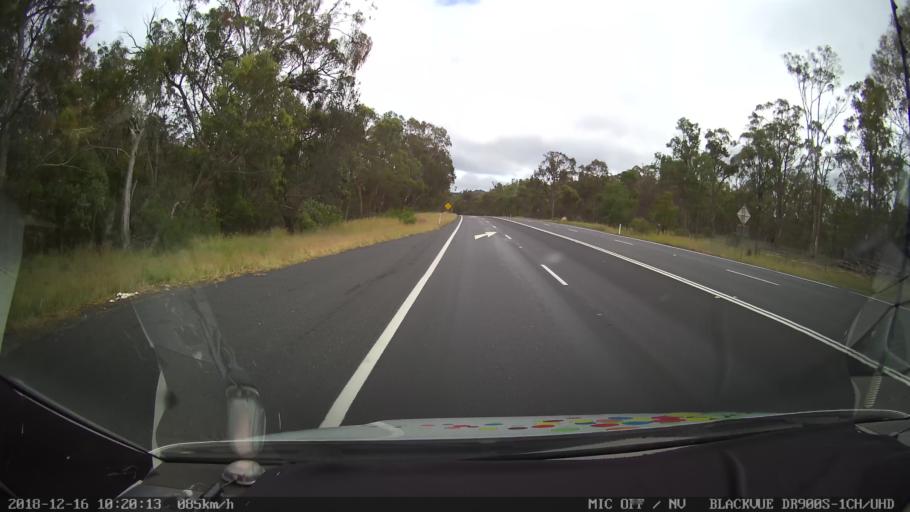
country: AU
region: New South Wales
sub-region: Tenterfield Municipality
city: Carrolls Creek
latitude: -29.2230
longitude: 152.0097
